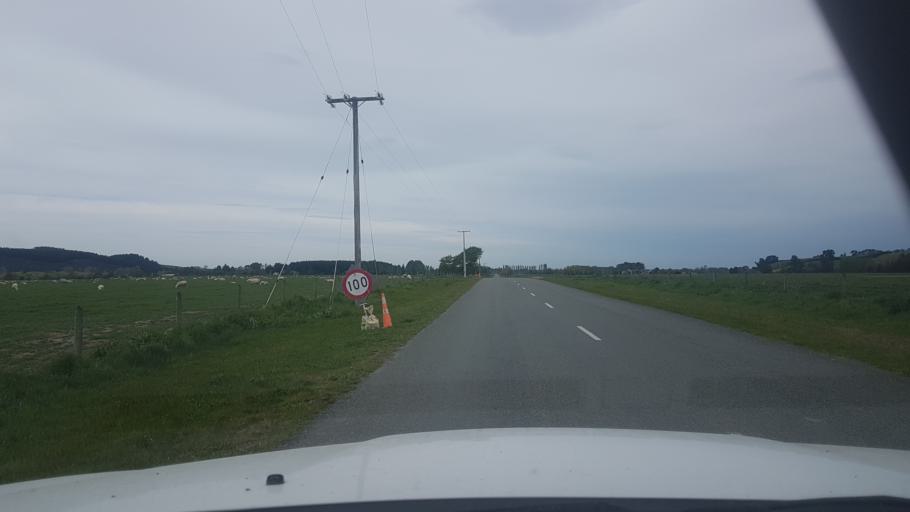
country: NZ
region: Canterbury
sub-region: Timaru District
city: Pleasant Point
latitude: -44.0851
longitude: 171.1825
